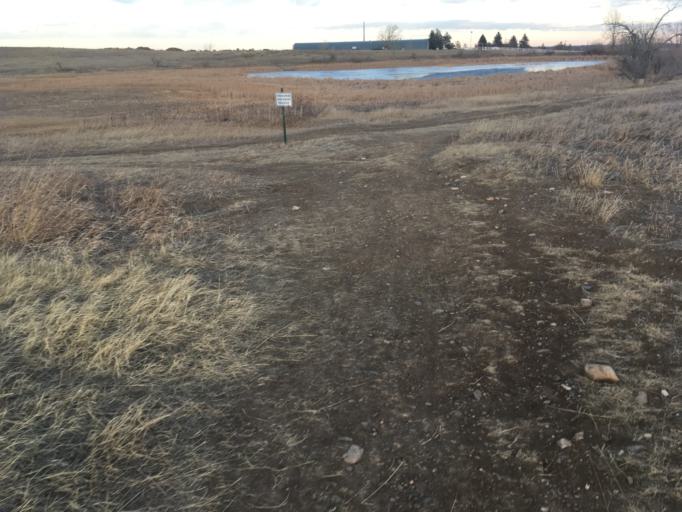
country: US
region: Colorado
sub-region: Boulder County
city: Superior
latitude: 39.8792
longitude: -105.1605
